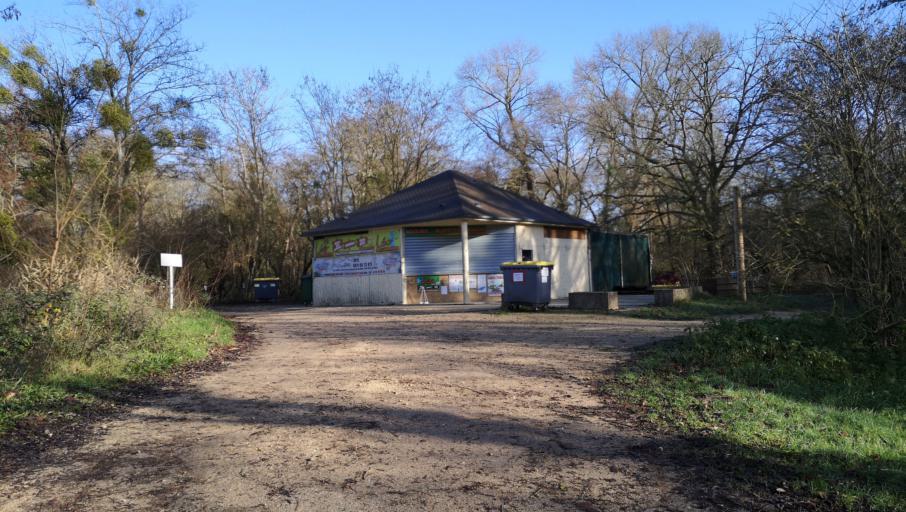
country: FR
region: Centre
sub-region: Departement du Loiret
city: Saint-Jean-le-Blanc
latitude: 47.8966
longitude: 1.9451
